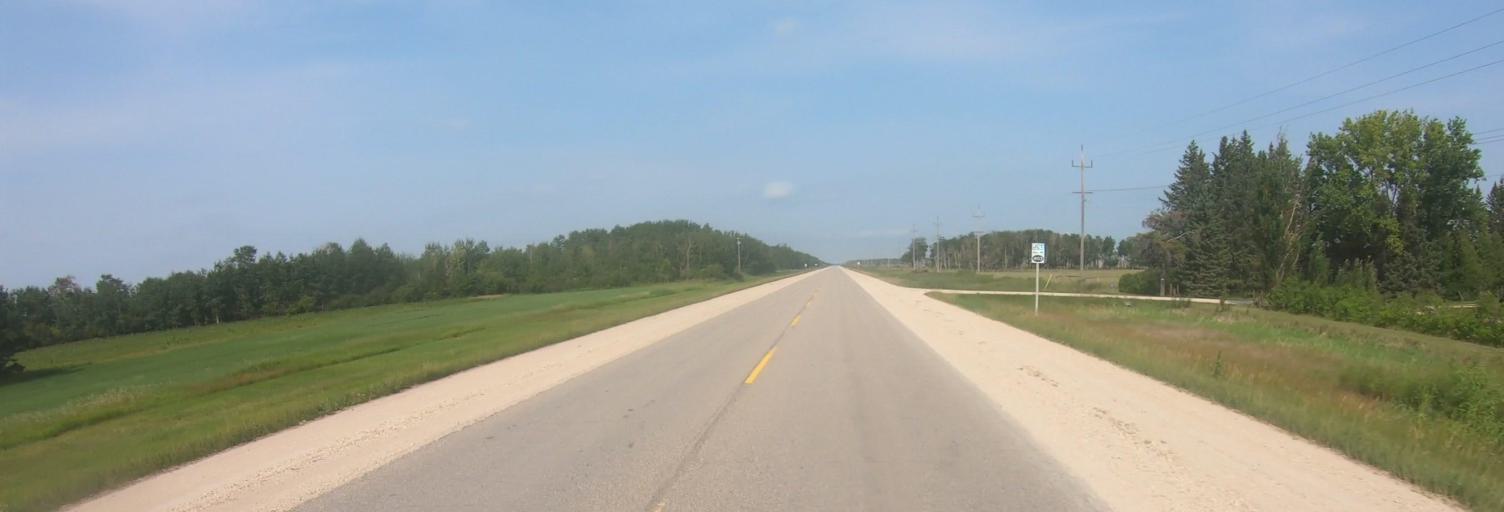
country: CA
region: Manitoba
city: La Broquerie
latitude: 49.3255
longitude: -96.5978
